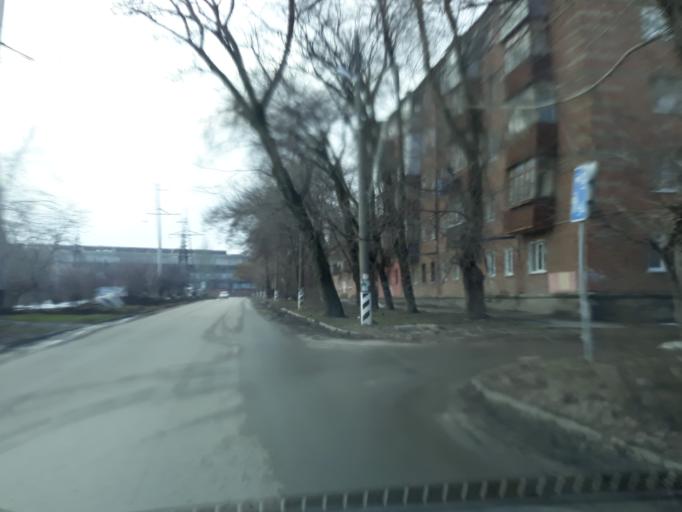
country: RU
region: Rostov
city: Taganrog
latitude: 47.2503
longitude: 38.9080
